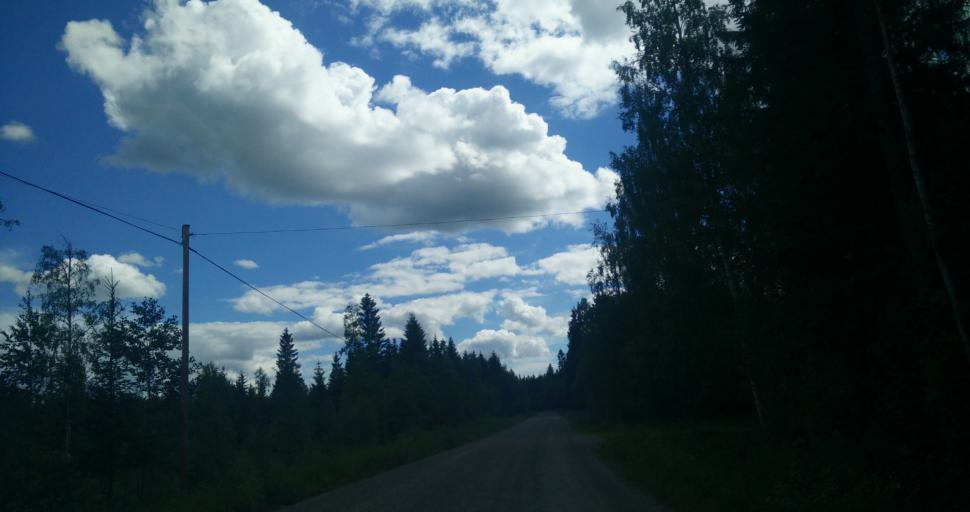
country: SE
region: Gaevleborg
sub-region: Nordanstigs Kommun
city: Bergsjoe
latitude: 62.0623
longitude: 16.7806
